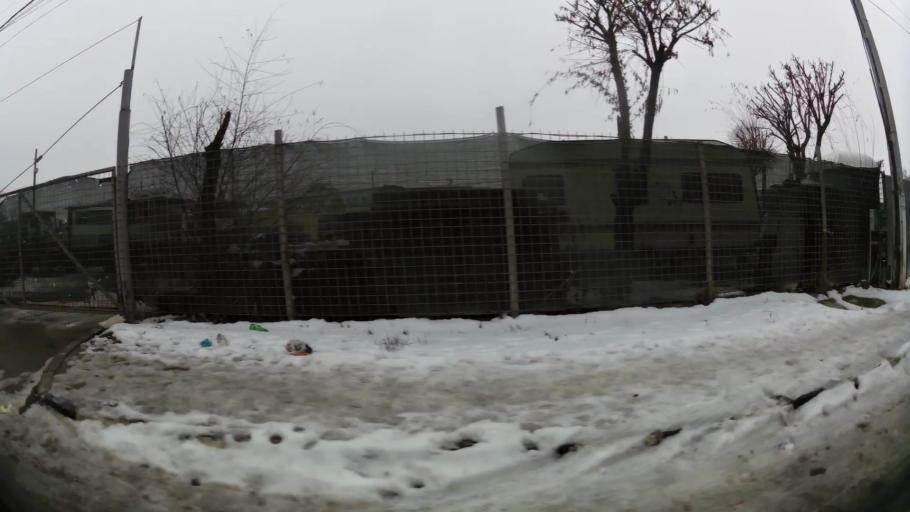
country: RO
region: Ilfov
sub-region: Comuna Chiajna
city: Chiajna
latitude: 44.4652
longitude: 25.9750
